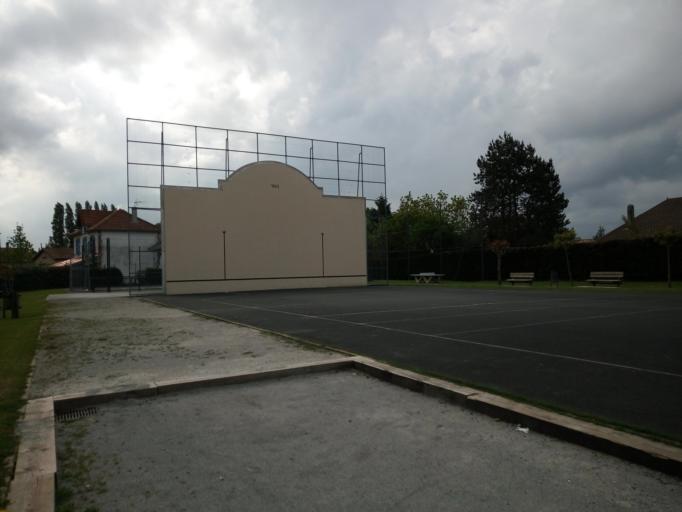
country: FR
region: Aquitaine
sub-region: Departement des Landes
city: Saint-Andre-de-Seignanx
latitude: 43.5517
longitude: -1.3077
